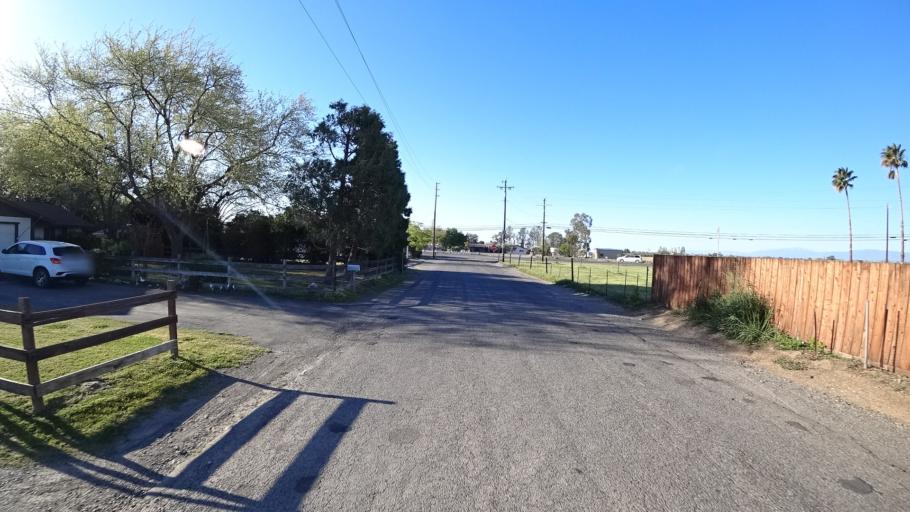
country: US
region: California
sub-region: Glenn County
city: Orland
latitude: 39.7555
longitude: -122.2156
